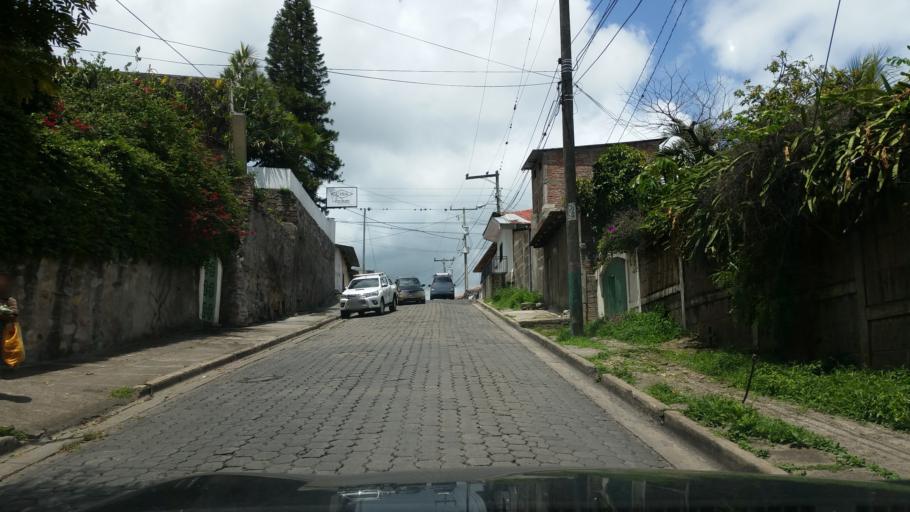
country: NI
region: Matagalpa
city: Matagalpa
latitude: 12.9262
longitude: -85.9158
